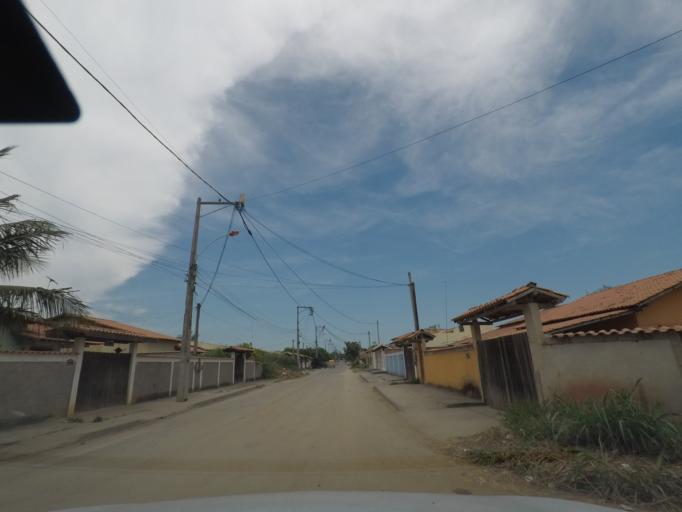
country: BR
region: Rio de Janeiro
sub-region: Niteroi
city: Niteroi
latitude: -22.9596
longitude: -42.9747
